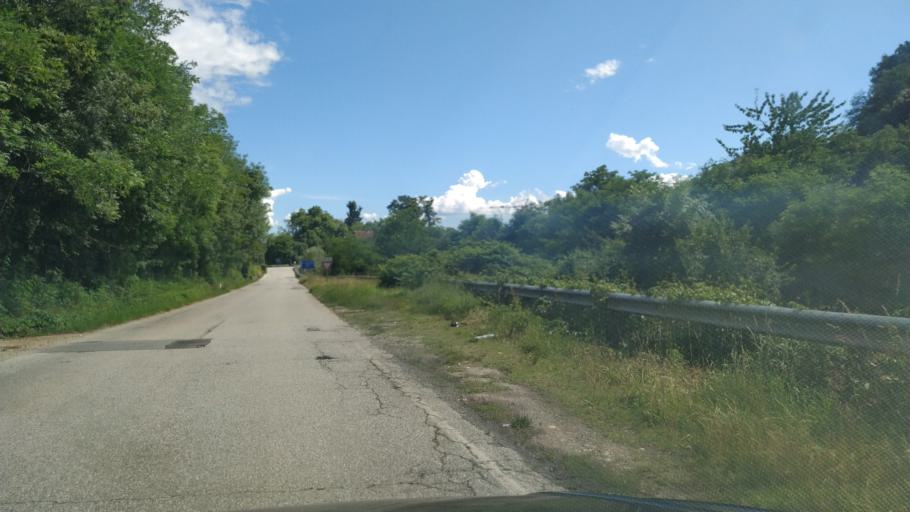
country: IT
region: Piedmont
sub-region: Provincia di Torino
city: Castellamonte
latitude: 45.3904
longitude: 7.7240
